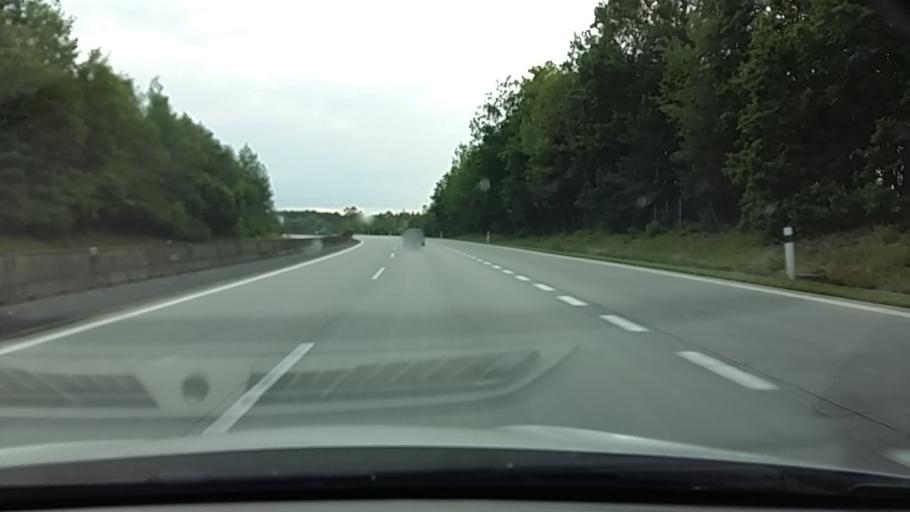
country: CZ
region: Plzensky
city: Vejprnice
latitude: 49.7097
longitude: 13.2769
